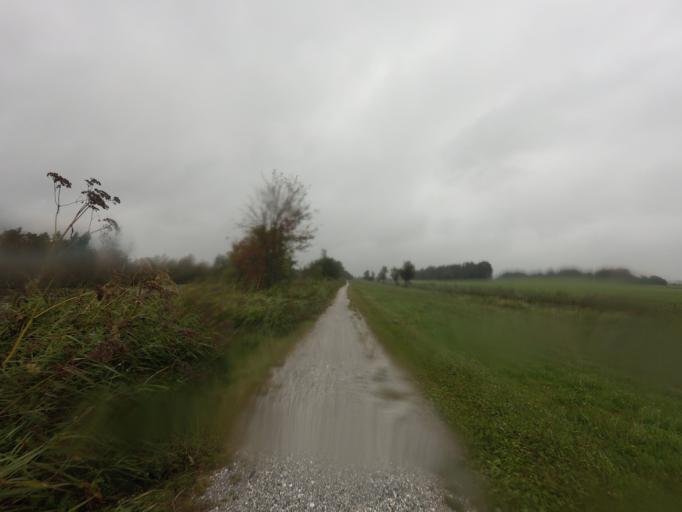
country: NL
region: Friesland
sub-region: Gemeente Smallingerland
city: Oudega
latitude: 53.0974
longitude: 5.9818
